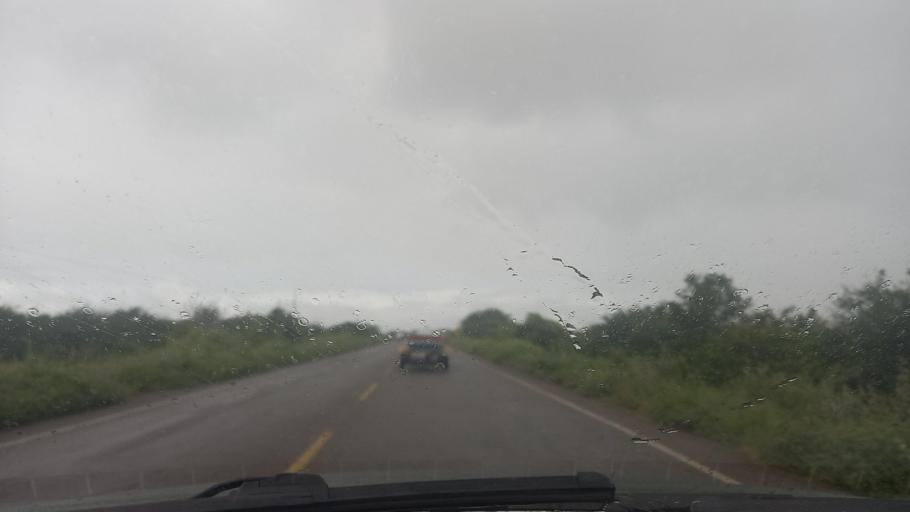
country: BR
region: Bahia
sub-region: Paulo Afonso
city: Paulo Afonso
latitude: -9.3519
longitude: -38.2785
